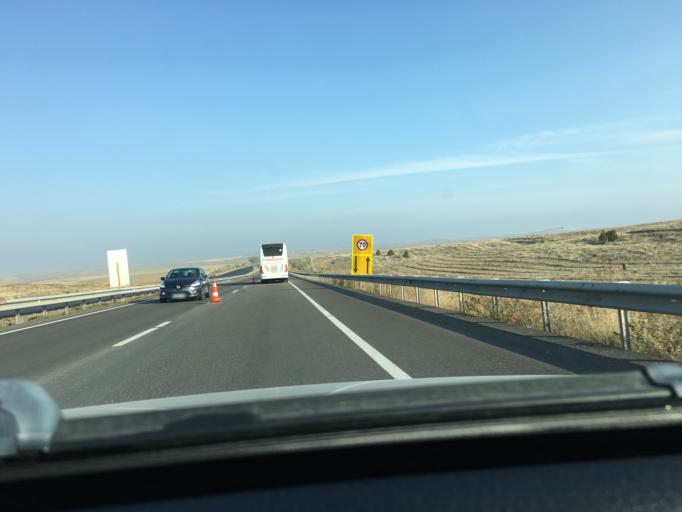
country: TR
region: Eskisehir
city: Gunyuzu
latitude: 39.5744
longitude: 31.8559
